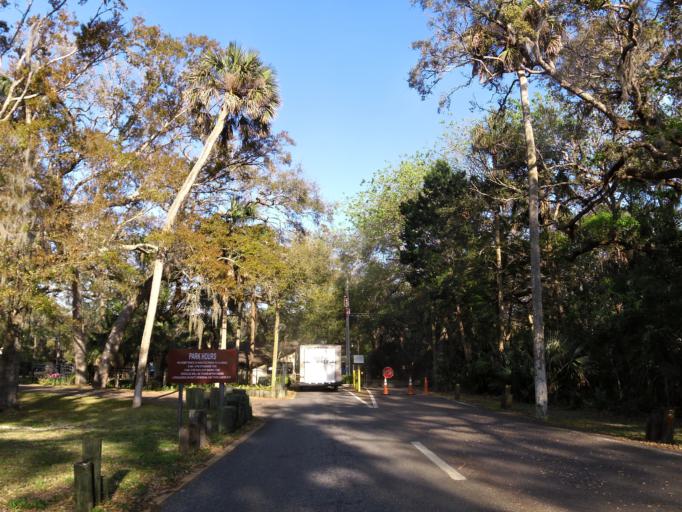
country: US
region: Florida
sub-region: Duval County
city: Atlantic Beach
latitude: 30.3713
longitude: -81.4074
